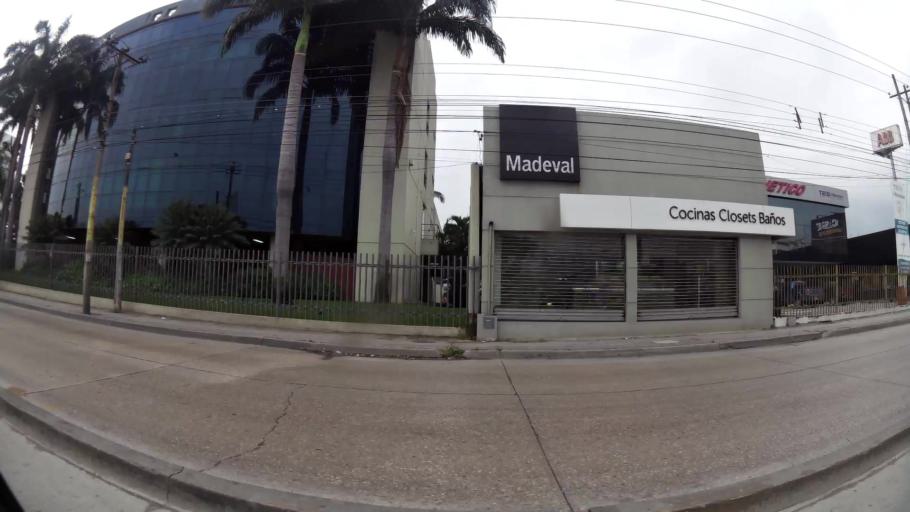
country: EC
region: Guayas
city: Eloy Alfaro
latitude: -2.1498
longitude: -79.9001
